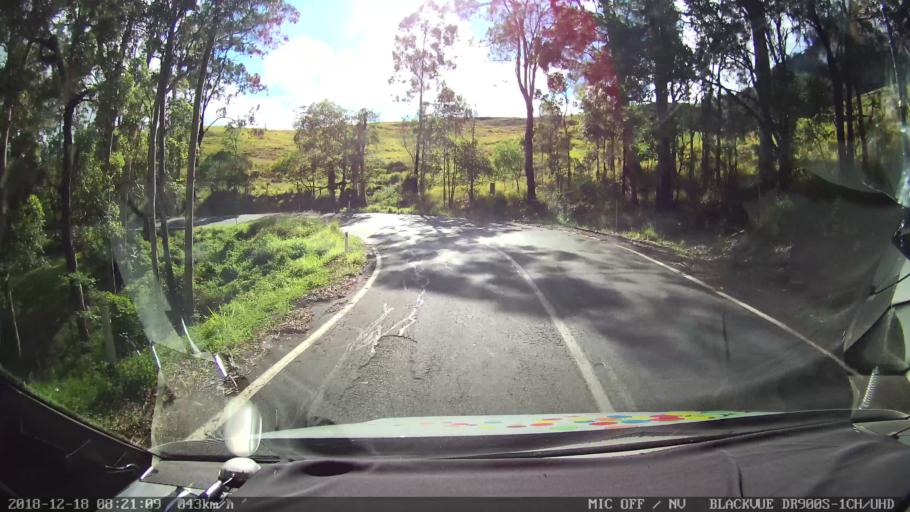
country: AU
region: New South Wales
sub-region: Kyogle
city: Kyogle
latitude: -28.3296
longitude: 152.7189
